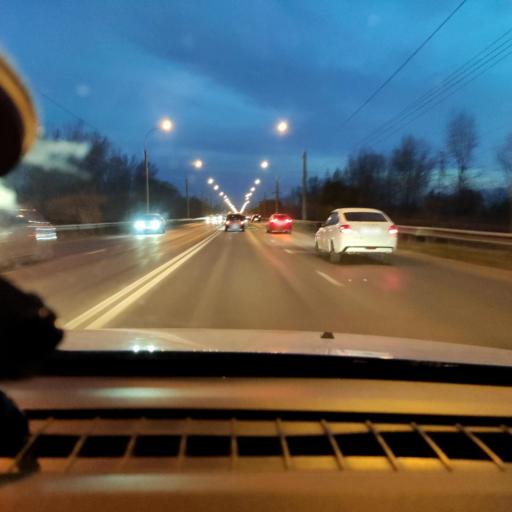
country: RU
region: Samara
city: Samara
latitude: 53.1512
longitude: 50.1868
